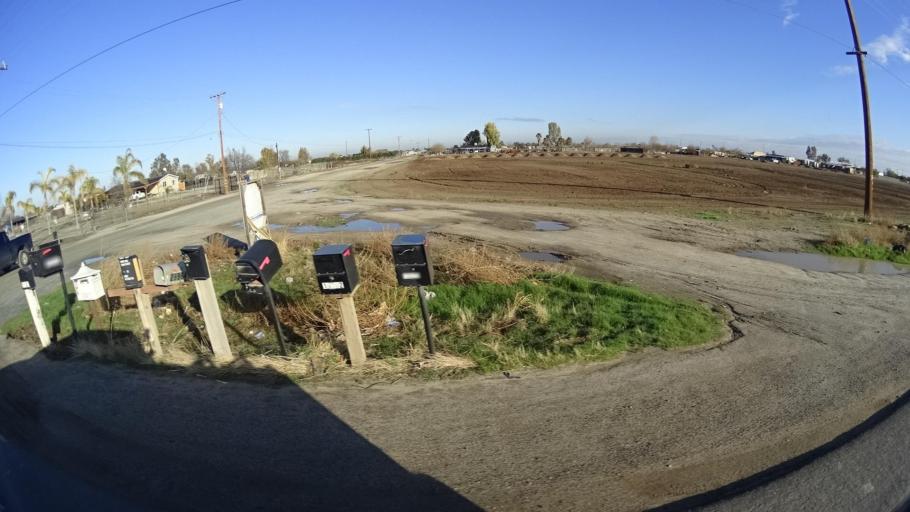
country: US
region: California
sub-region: Kern County
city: Delano
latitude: 35.7759
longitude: -119.2983
